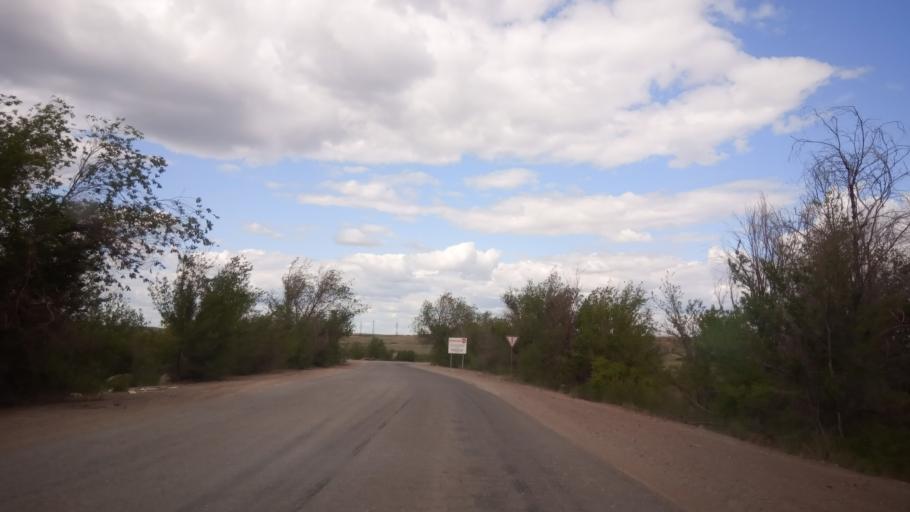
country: RU
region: Orenburg
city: Novotroitsk
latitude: 51.2521
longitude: 58.3662
